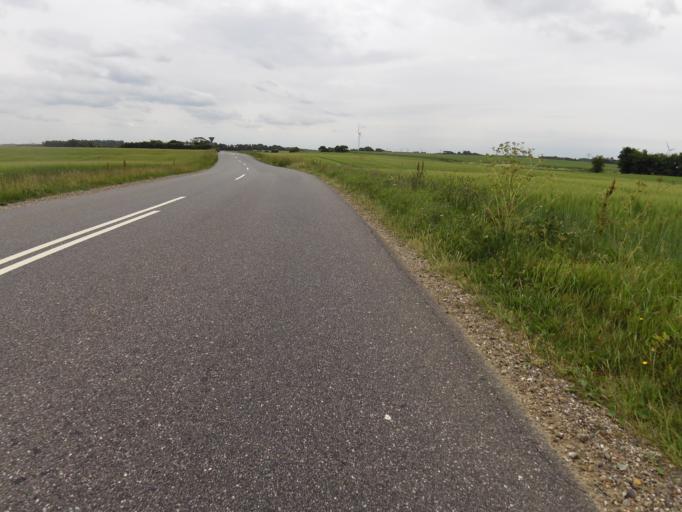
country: DK
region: Central Jutland
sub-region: Holstebro Kommune
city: Holstebro
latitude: 56.4141
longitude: 8.6968
